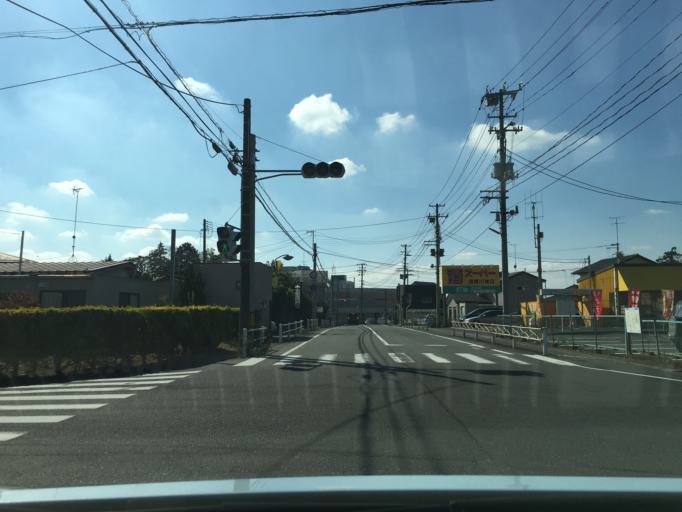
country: JP
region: Fukushima
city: Sukagawa
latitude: 37.2846
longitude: 140.3886
